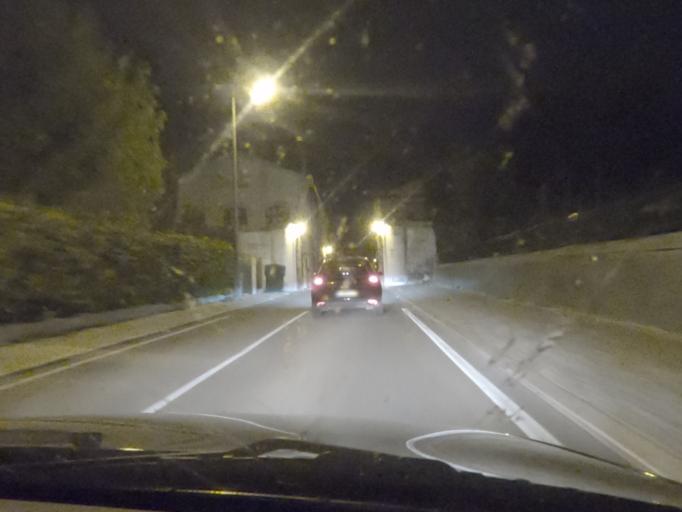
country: PT
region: Evora
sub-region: Estremoz
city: Estremoz
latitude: 38.8457
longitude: -7.5916
